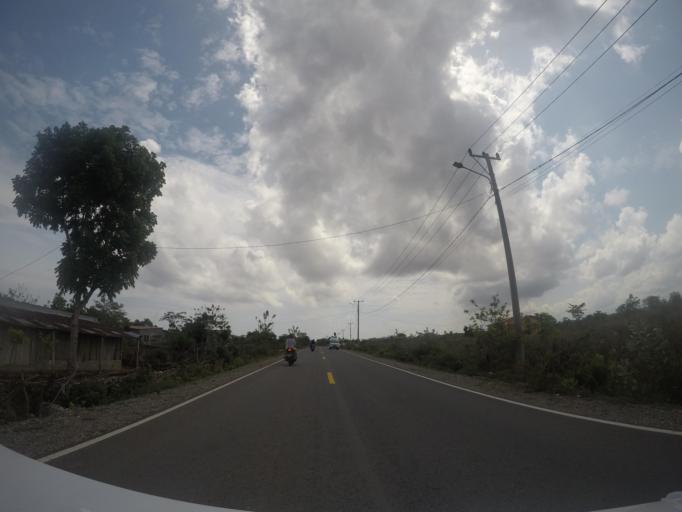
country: TL
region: Baucau
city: Baucau
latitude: -8.4758
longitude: 126.4045
